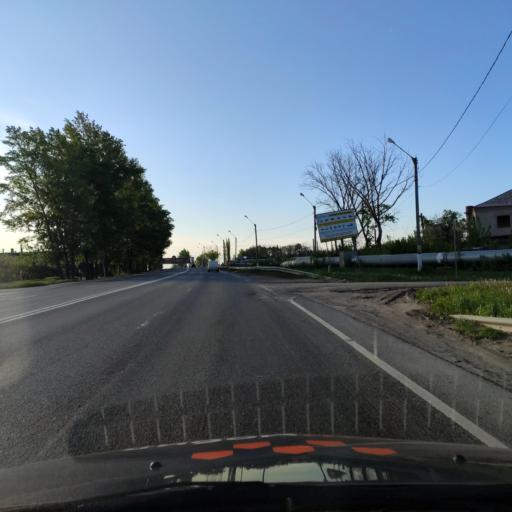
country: RU
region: Lipetsk
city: Yelets
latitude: 52.5961
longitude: 38.4788
